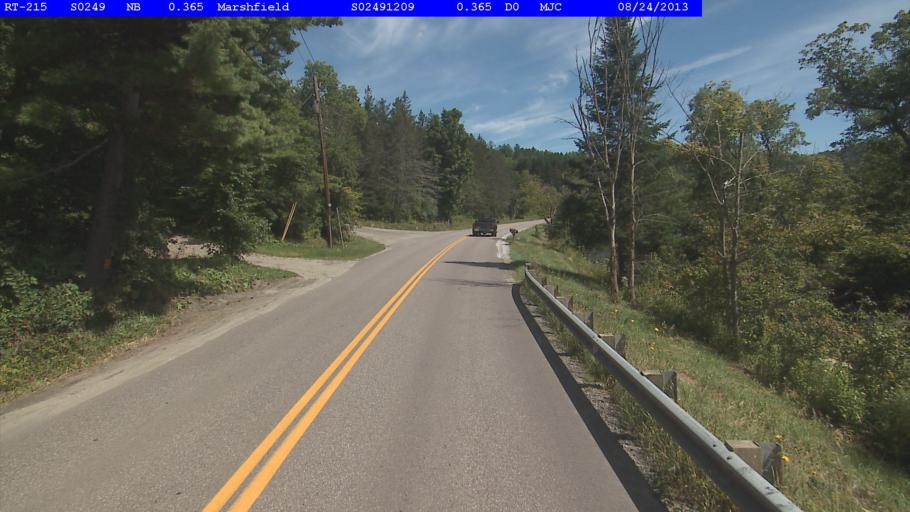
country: US
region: Vermont
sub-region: Caledonia County
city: Hardwick
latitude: 44.3558
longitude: -72.3446
